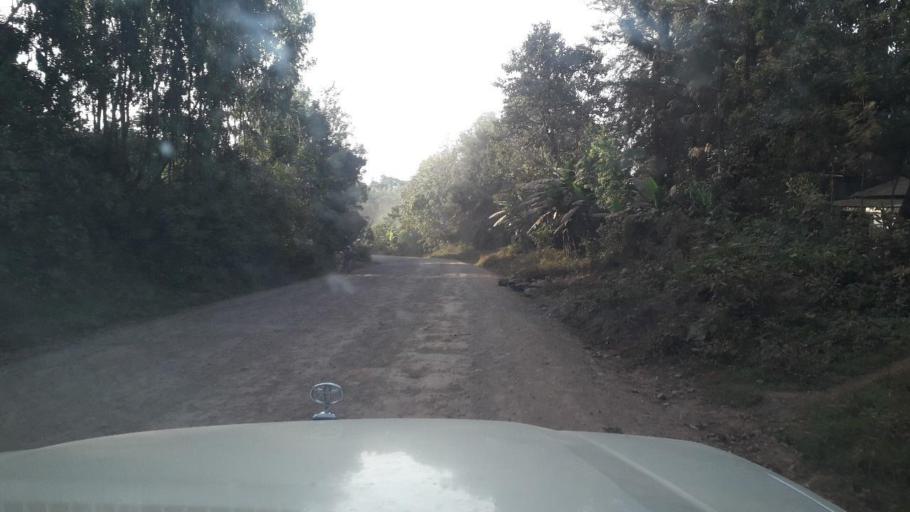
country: ET
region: Oromiya
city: Jima
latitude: 7.6011
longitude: 36.8441
